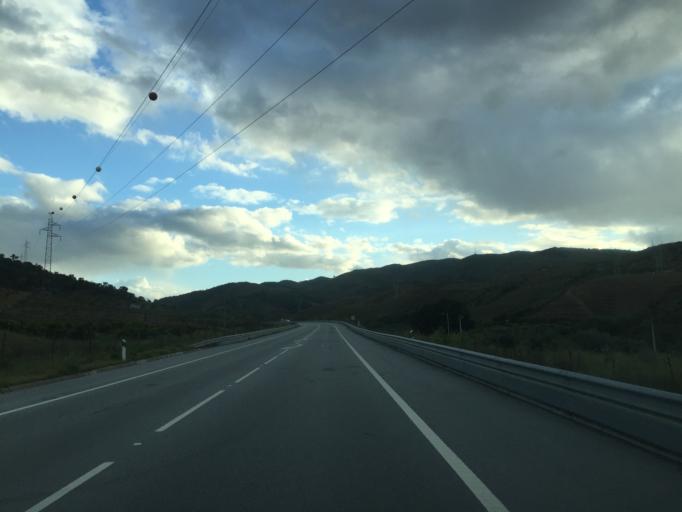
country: PT
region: Guarda
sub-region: Vila Nova de Foz Coa
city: Vila Nova de Foz Coa
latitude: 41.1071
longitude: -7.1391
